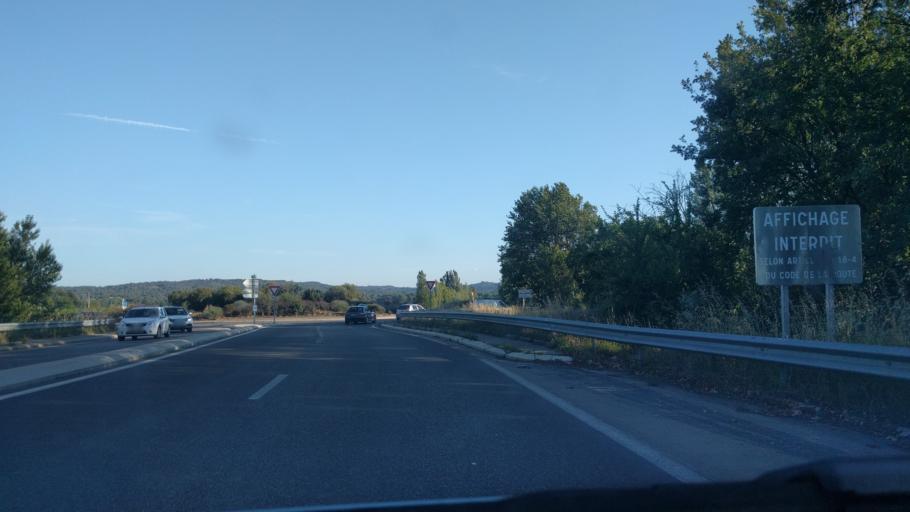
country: FR
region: Provence-Alpes-Cote d'Azur
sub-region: Departement du Vaucluse
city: Pertuis
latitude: 43.6609
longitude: 5.4948
